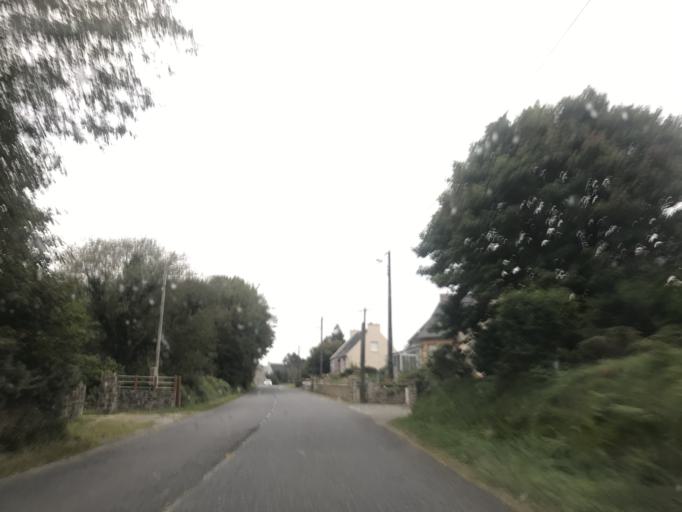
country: FR
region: Brittany
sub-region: Departement du Finistere
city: Plouneour-Menez
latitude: 48.4088
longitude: -3.9572
